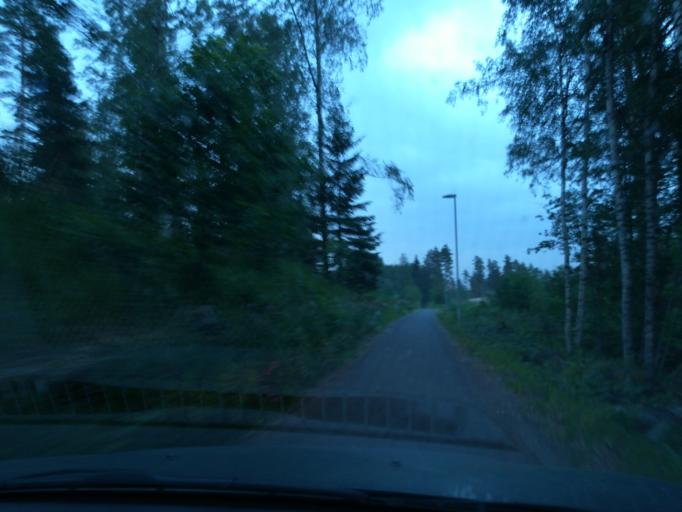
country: FI
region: Southern Savonia
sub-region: Mikkeli
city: Ristiina
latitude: 61.4950
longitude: 27.2718
